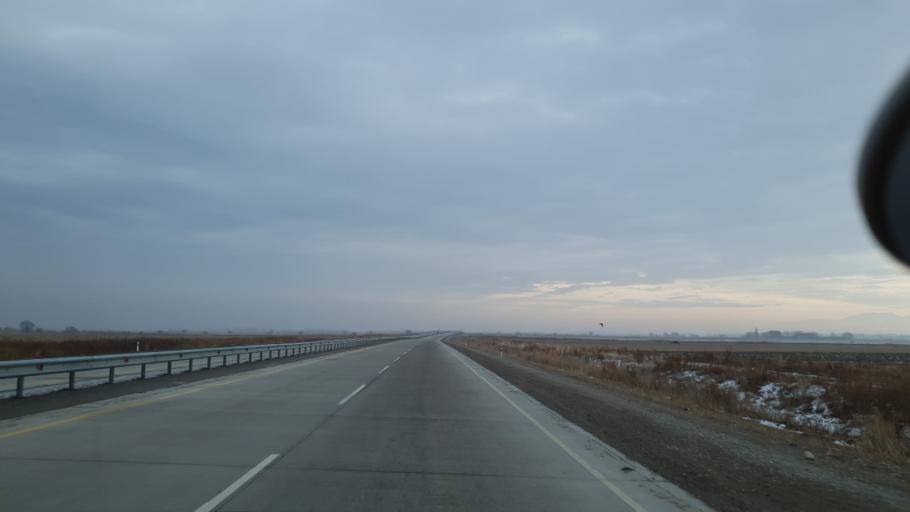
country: KZ
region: Almaty Oblysy
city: Talghar
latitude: 43.4662
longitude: 77.2856
